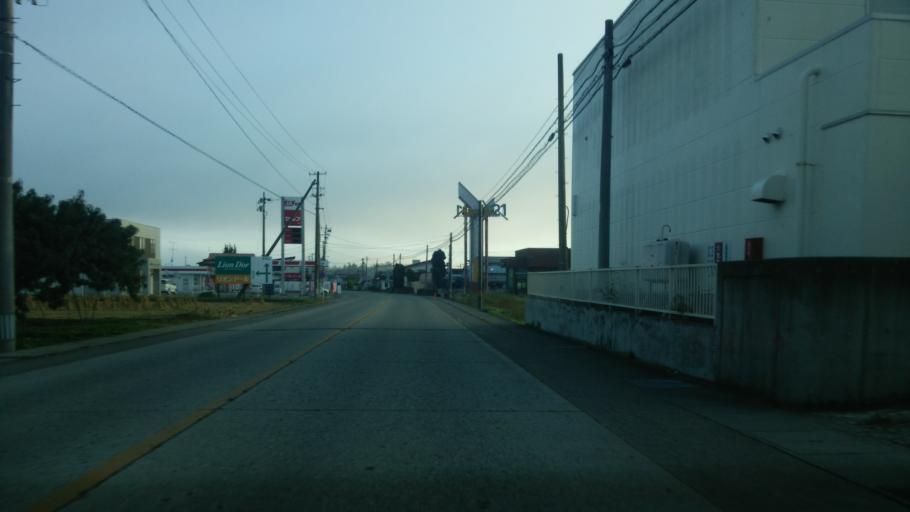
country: JP
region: Fukushima
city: Kitakata
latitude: 37.4490
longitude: 139.8340
